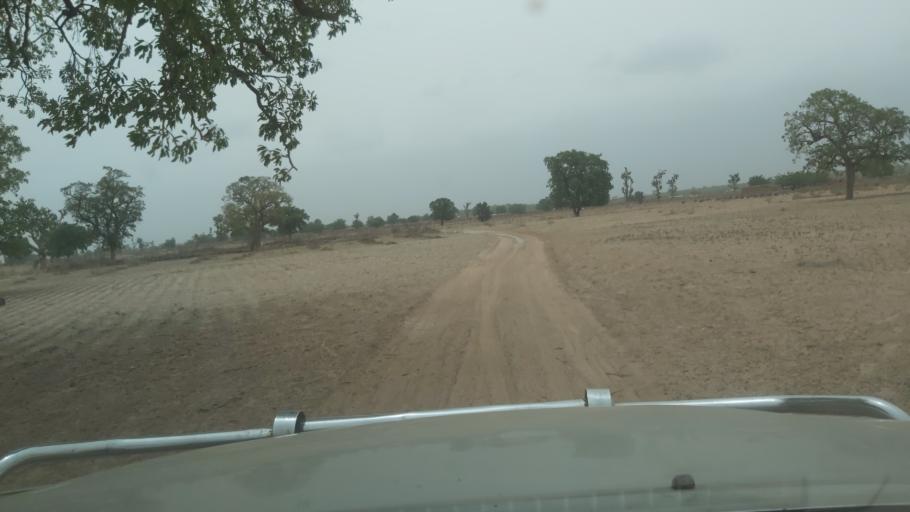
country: ML
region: Koulikoro
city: Banamba
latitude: 13.3768
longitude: -7.2284
